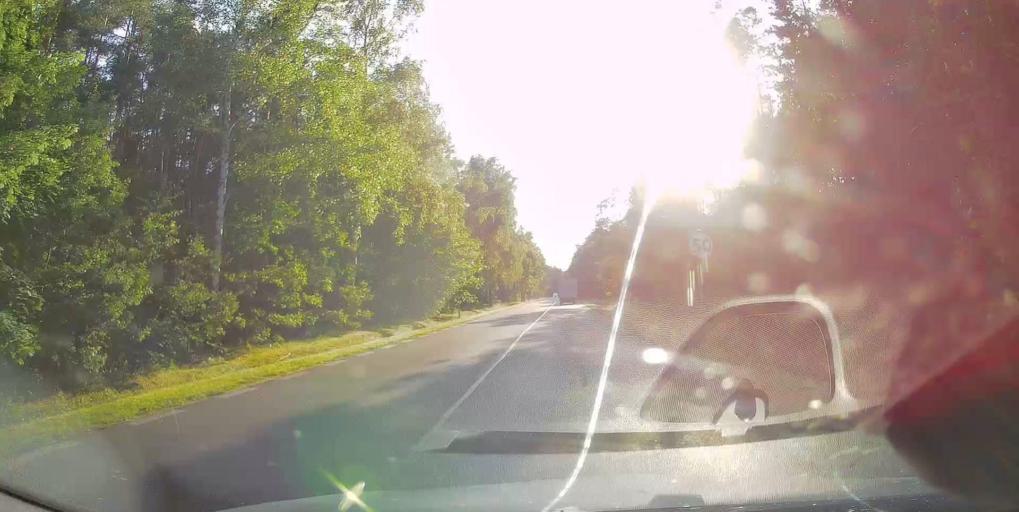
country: PL
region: Lodz Voivodeship
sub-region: Powiat rawski
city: Regnow
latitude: 51.7988
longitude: 20.3962
